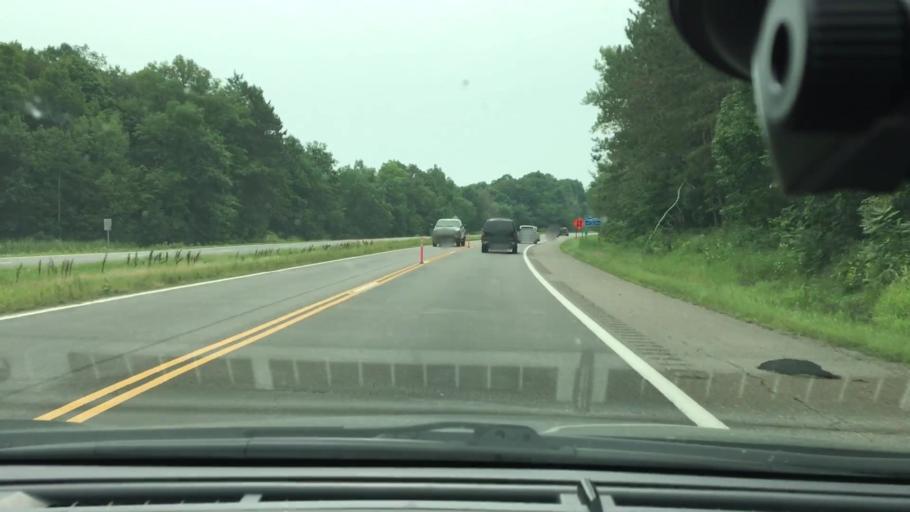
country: US
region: Minnesota
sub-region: Mille Lacs County
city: Vineland
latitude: 46.2843
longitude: -93.8209
